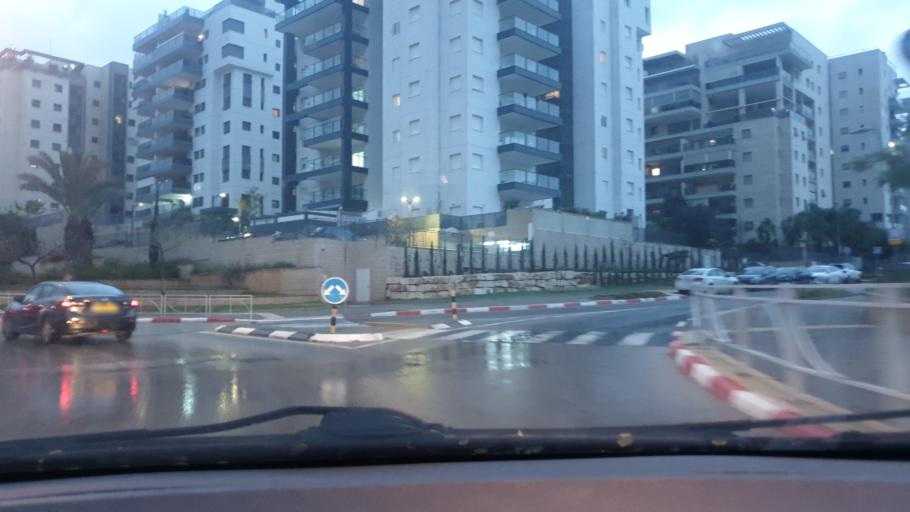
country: IL
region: Central District
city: Rishon LeZiyyon
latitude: 31.9815
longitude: 34.8074
